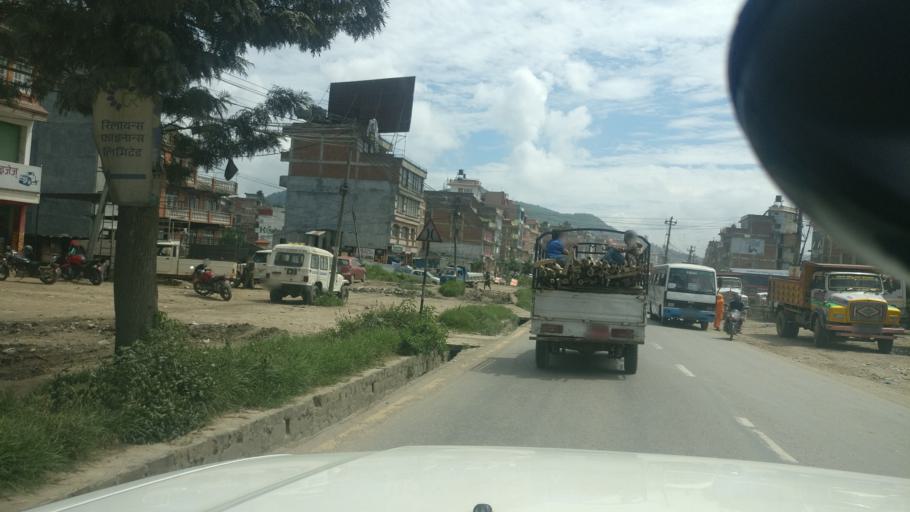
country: NP
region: Central Region
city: Banepa
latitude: 27.6321
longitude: 85.5136
